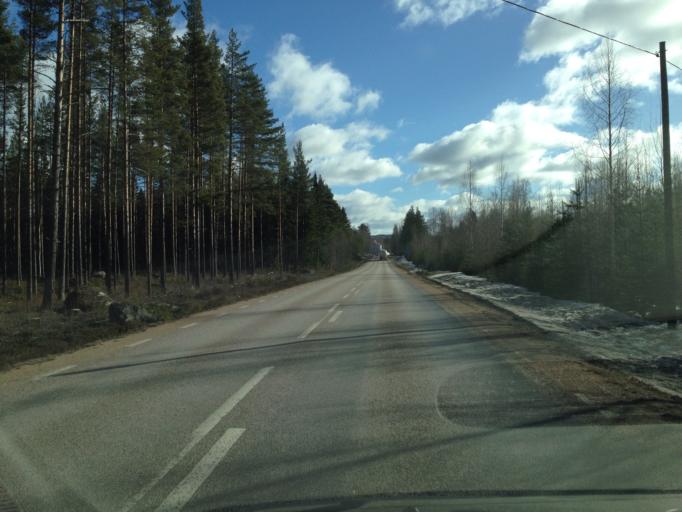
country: SE
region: Gaevleborg
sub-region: Ljusdals Kommun
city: Farila
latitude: 61.9874
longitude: 15.2862
